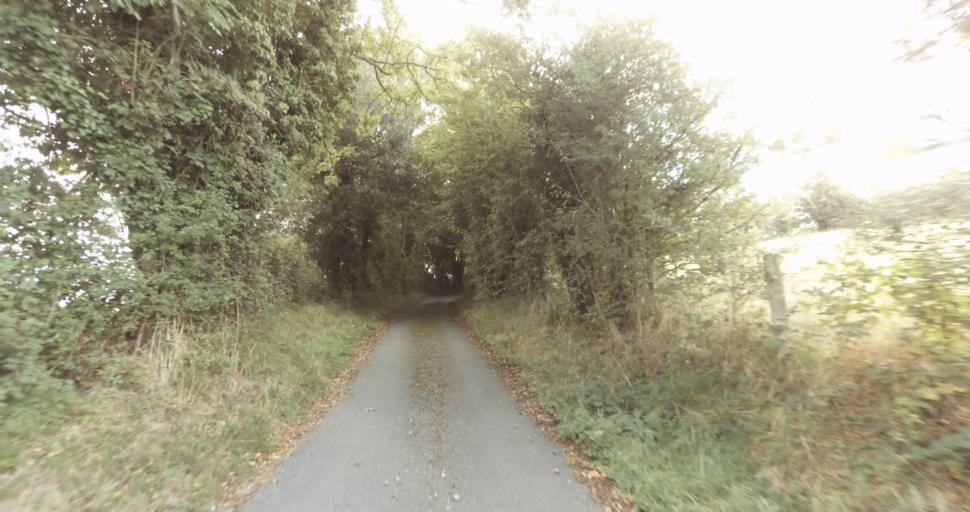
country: FR
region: Lower Normandy
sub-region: Departement de l'Orne
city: Vimoutiers
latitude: 48.8888
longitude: 0.2228
